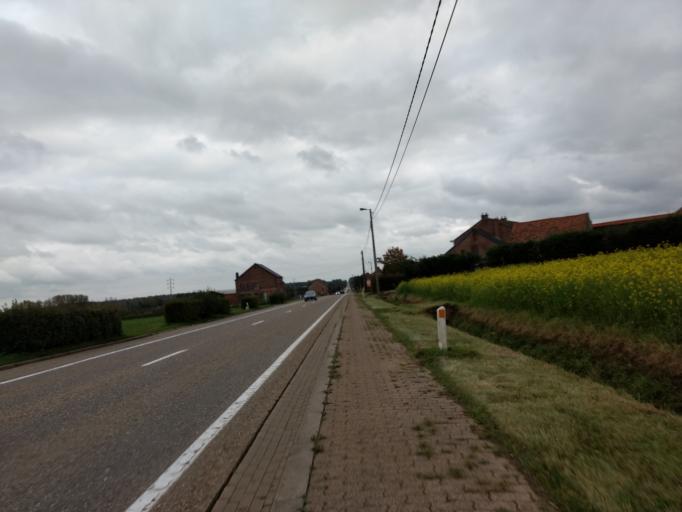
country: BE
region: Flanders
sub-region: Provincie Vlaams-Brabant
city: Bekkevoort
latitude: 50.9344
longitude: 4.9893
